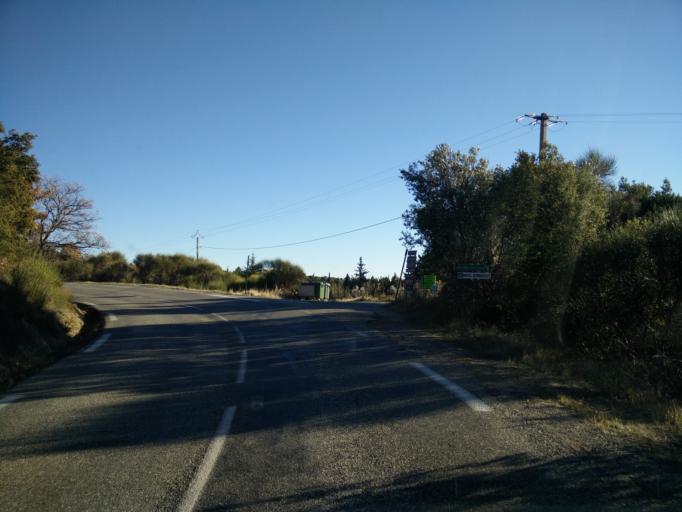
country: FR
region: Provence-Alpes-Cote d'Azur
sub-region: Departement du Var
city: Villecroze
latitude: 43.5948
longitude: 6.2836
